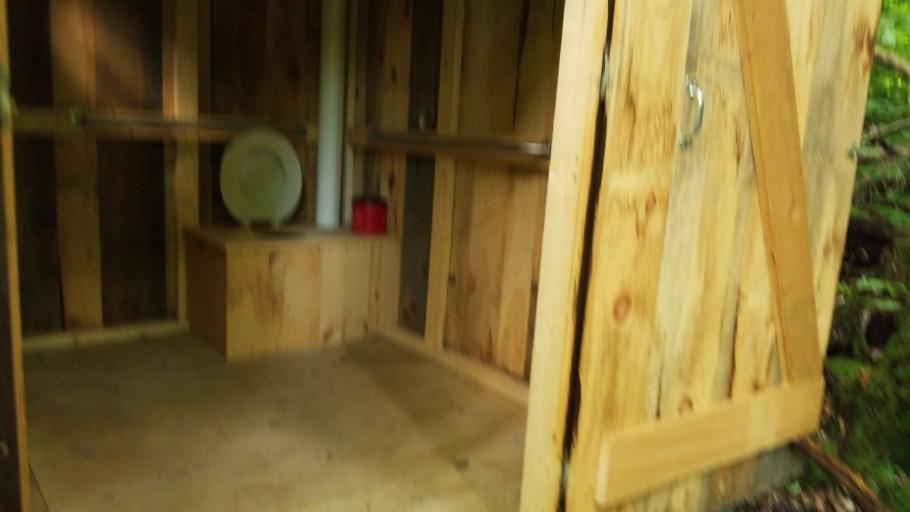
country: US
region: New York
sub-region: St. Lawrence County
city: Gouverneur
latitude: 44.1611
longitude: -75.3736
